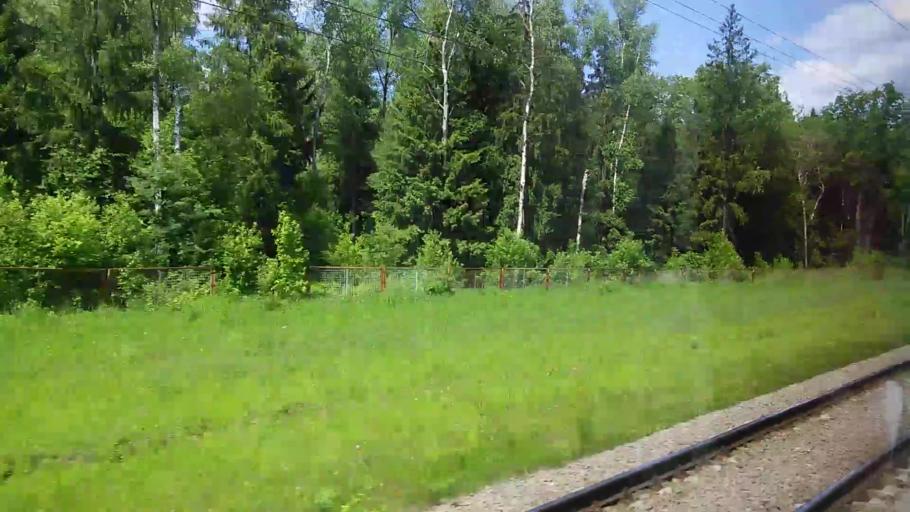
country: RU
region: Moskovskaya
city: Lobnya
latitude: 55.9917
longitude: 37.4737
